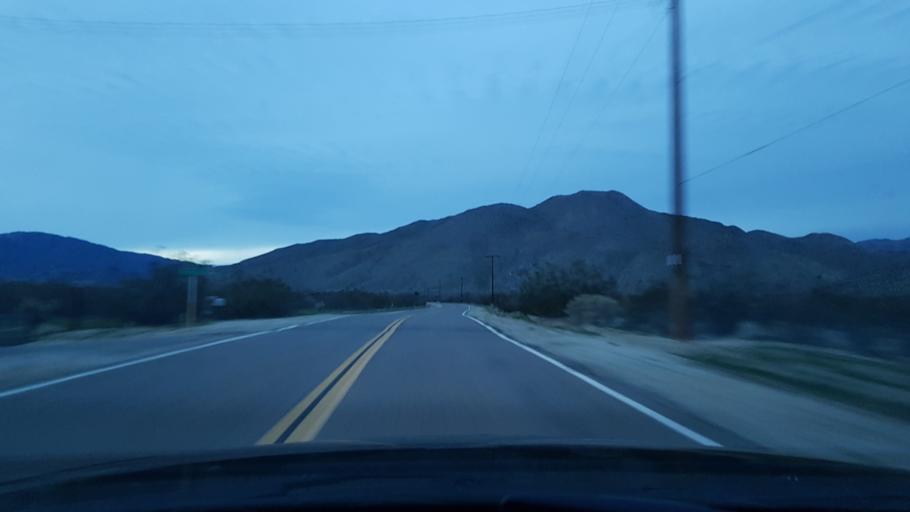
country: US
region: California
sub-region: San Diego County
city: Julian
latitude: 33.0861
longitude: -116.4481
